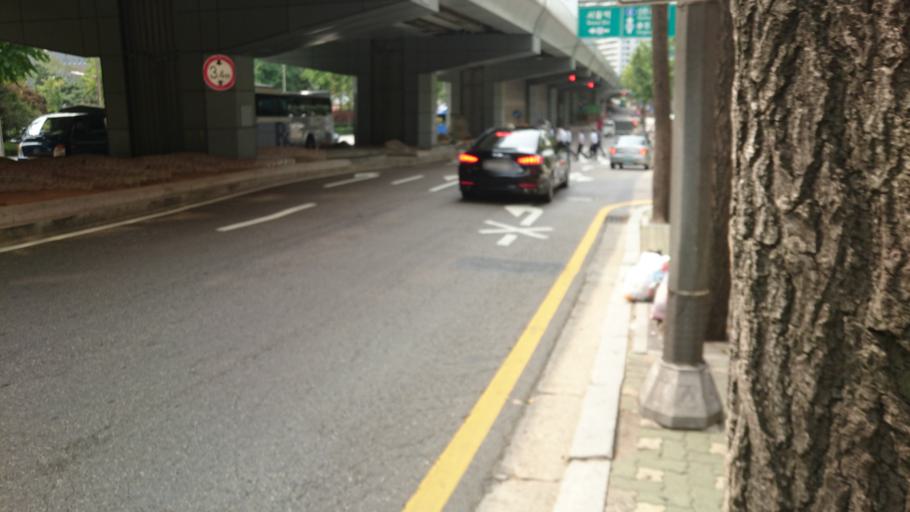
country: KR
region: Seoul
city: Seoul
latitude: 37.5614
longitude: 126.9703
